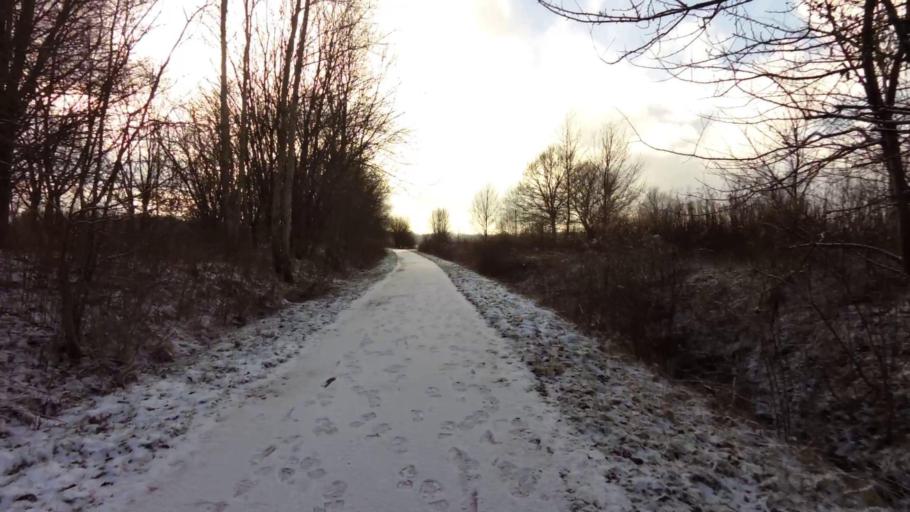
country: PL
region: West Pomeranian Voivodeship
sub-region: Powiat swidwinski
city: Polczyn-Zdroj
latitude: 53.7696
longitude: 16.0711
